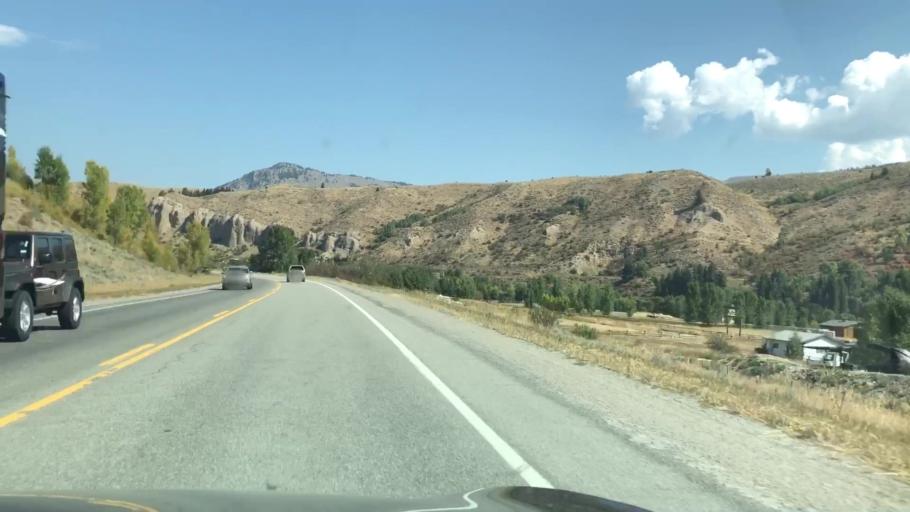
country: US
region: Wyoming
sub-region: Teton County
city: Hoback
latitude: 43.3495
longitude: -110.7208
